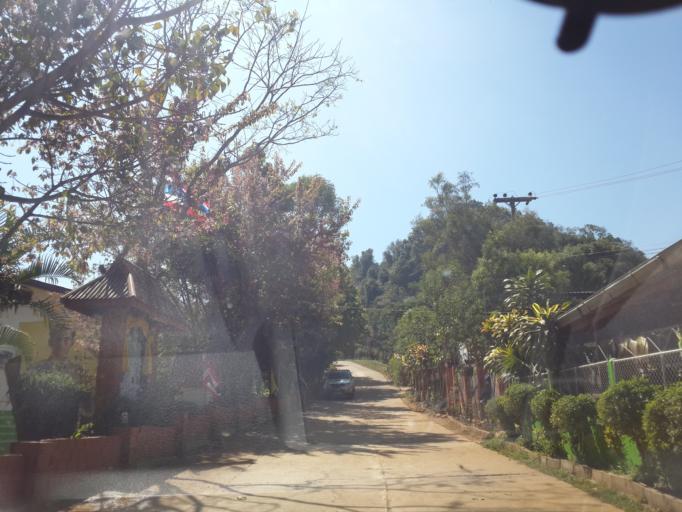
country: TH
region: Chiang Mai
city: Fang
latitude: 19.9261
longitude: 99.0519
